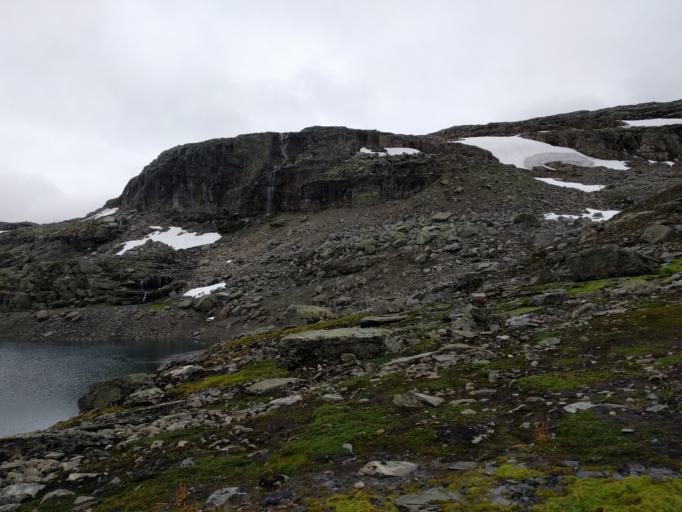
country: NO
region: Aust-Agder
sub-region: Bykle
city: Hovden
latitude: 59.8829
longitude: 7.0479
